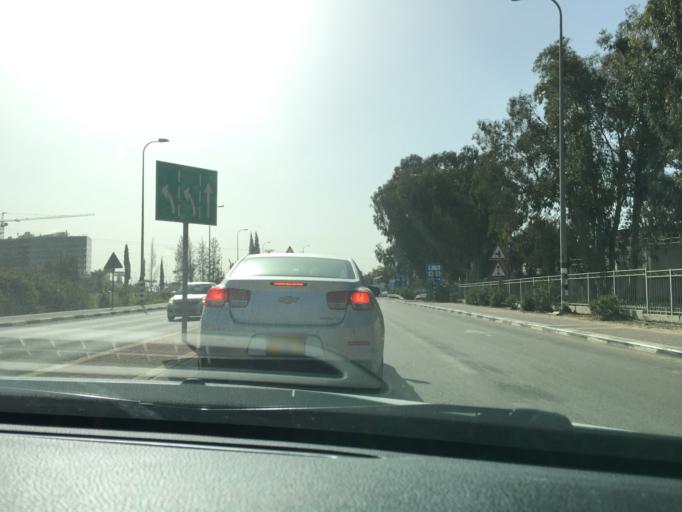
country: IL
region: Central District
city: Kfar Saba
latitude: 32.1717
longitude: 34.9302
